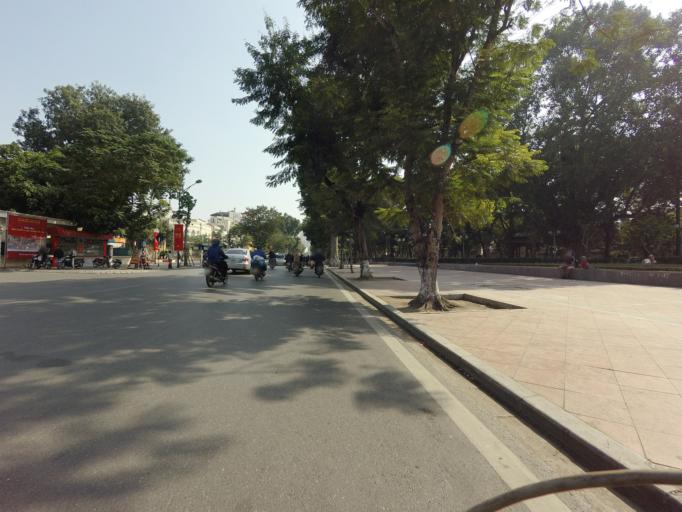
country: VN
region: Ha Noi
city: Hanoi
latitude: 21.0318
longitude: 105.8399
